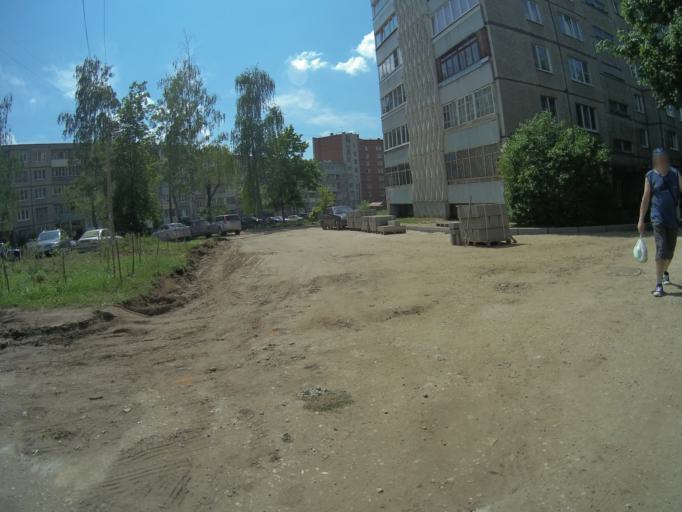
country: RU
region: Vladimir
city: Vladimir
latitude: 56.1255
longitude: 40.3468
